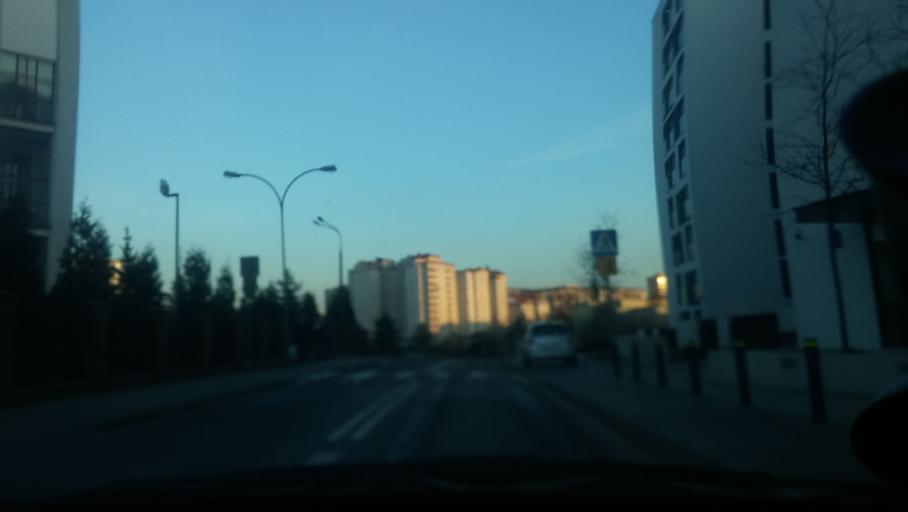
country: PL
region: Masovian Voivodeship
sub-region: Warszawa
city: Praga Poludnie
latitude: 52.2295
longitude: 21.0844
